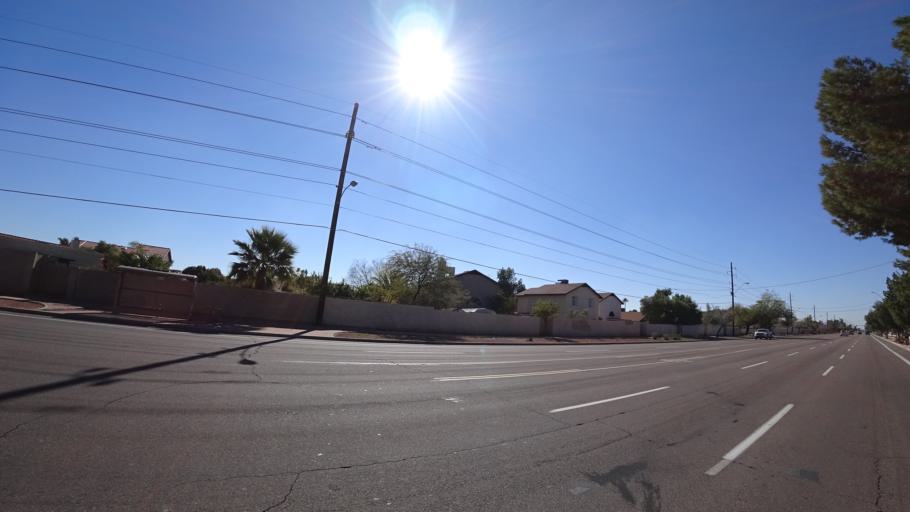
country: US
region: Arizona
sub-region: Maricopa County
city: Peoria
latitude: 33.6547
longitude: -112.1388
